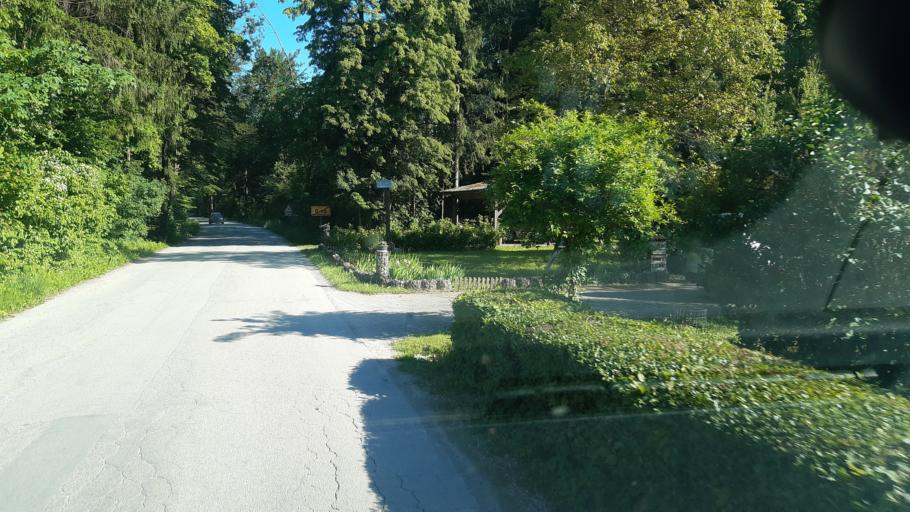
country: SI
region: Sencur
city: Hrastje
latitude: 46.2081
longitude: 14.3914
